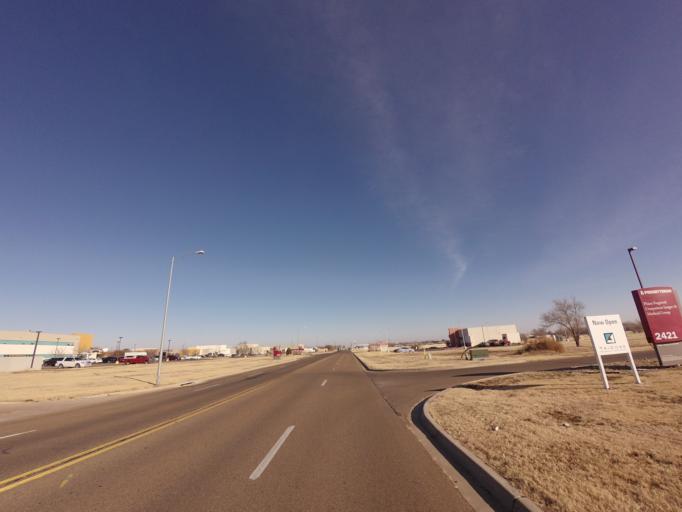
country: US
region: New Mexico
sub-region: Curry County
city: Clovis
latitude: 34.4192
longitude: -103.2371
